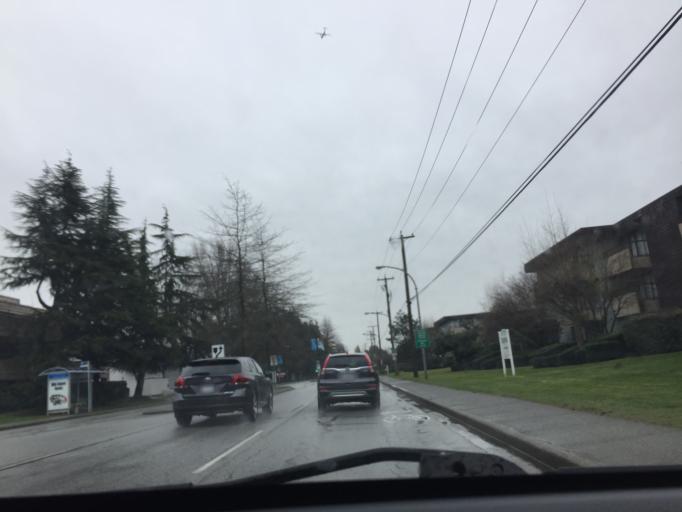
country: CA
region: British Columbia
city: Richmond
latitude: 49.1688
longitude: -123.1478
